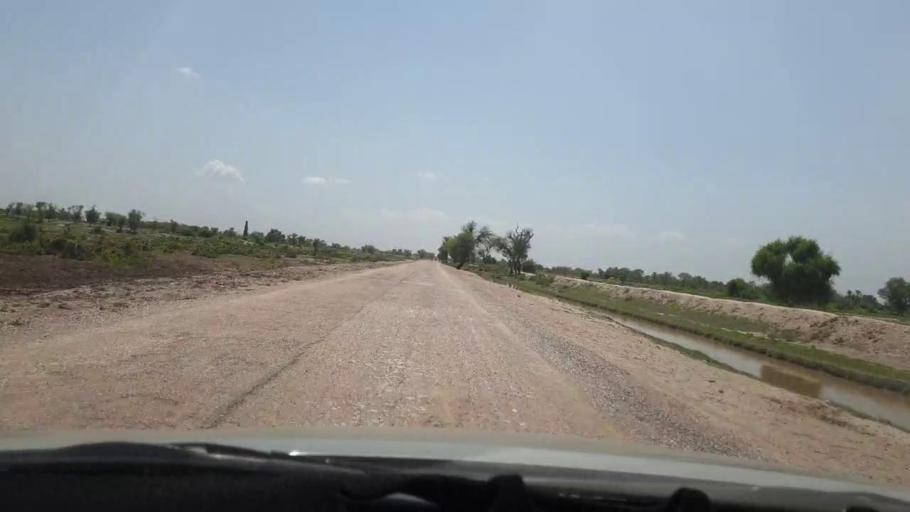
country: PK
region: Sindh
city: Pano Aqil
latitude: 27.7249
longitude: 69.1788
